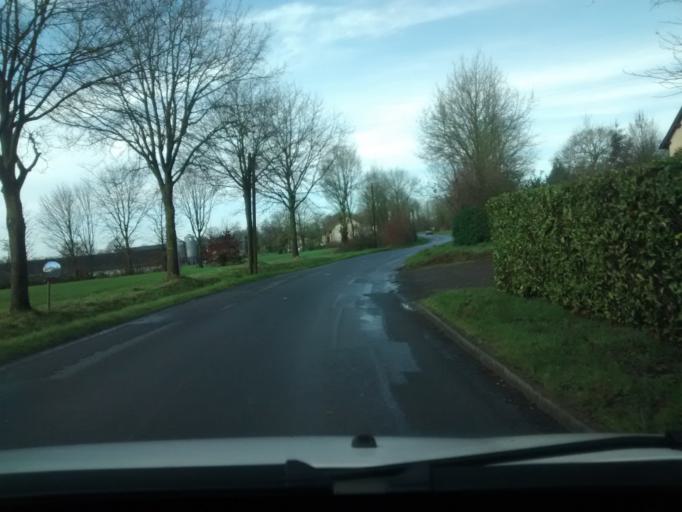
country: FR
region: Brittany
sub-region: Departement d'Ille-et-Vilaine
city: Vezin-le-Coquet
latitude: 48.1455
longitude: -1.7428
